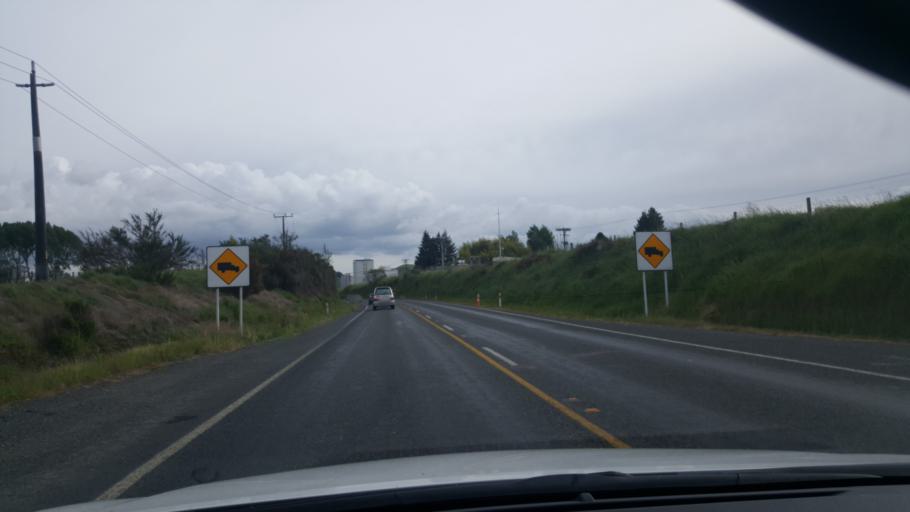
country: NZ
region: Bay of Plenty
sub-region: Rotorua District
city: Rotorua
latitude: -38.4209
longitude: 176.3180
